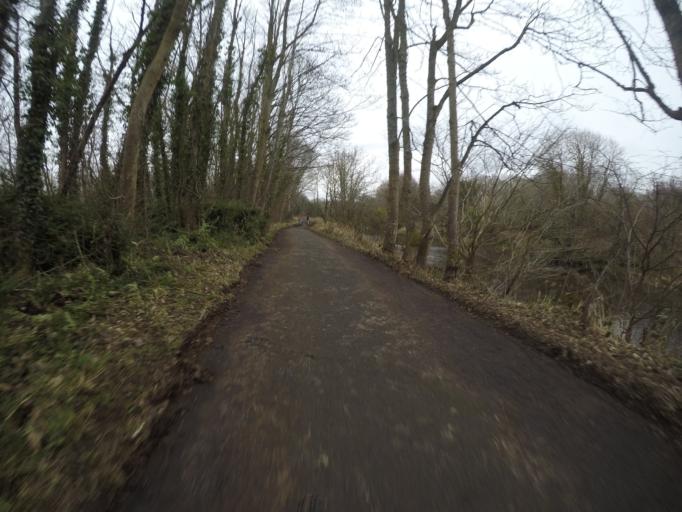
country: GB
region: Scotland
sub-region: North Ayrshire
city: Kilwinning
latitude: 55.6419
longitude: -4.6870
